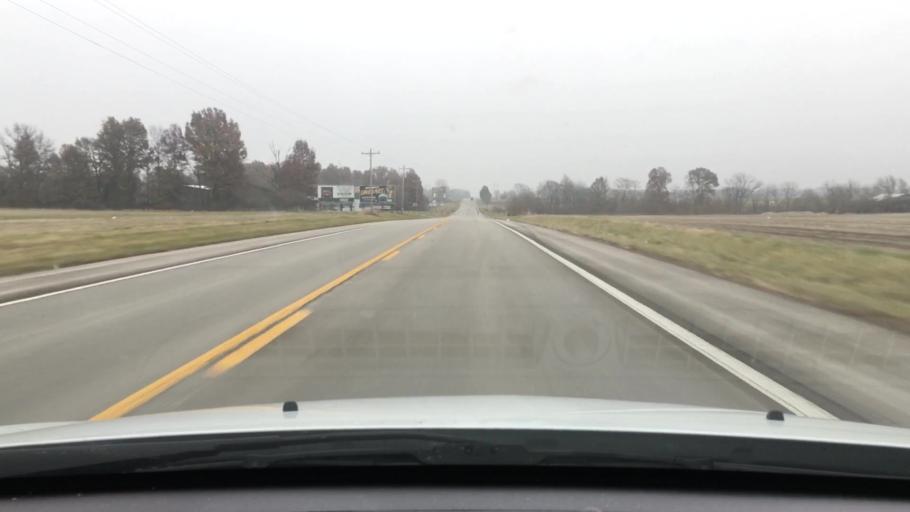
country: US
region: Missouri
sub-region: Audrain County
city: Mexico
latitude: 39.1637
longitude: -91.8122
